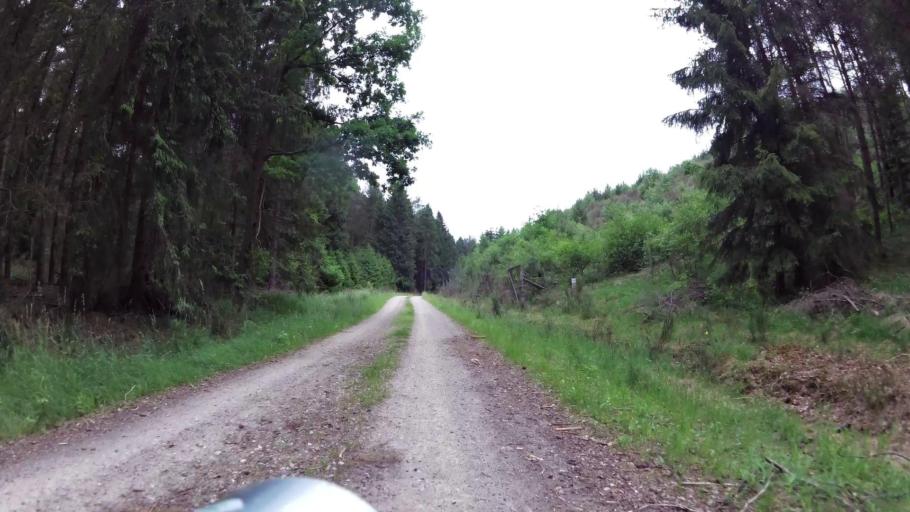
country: PL
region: West Pomeranian Voivodeship
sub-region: Powiat szczecinecki
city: Bialy Bor
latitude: 53.9481
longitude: 16.8288
